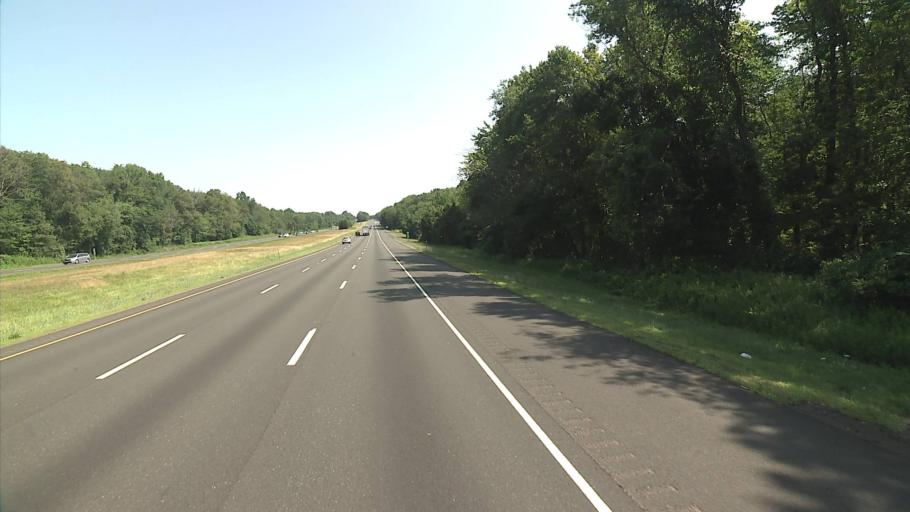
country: US
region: Connecticut
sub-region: New Haven County
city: Wallingford Center
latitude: 41.4692
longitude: -72.7739
